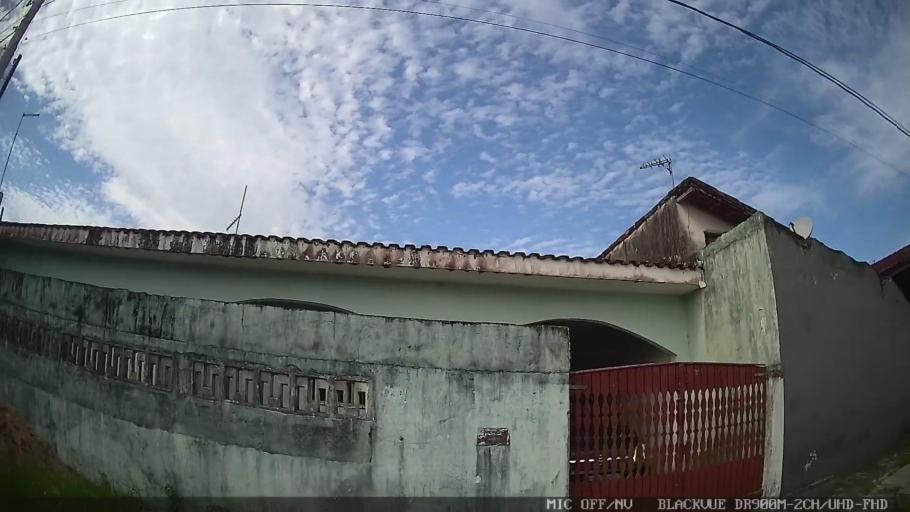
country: BR
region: Sao Paulo
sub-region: Itanhaem
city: Itanhaem
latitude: -24.1566
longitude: -46.7531
